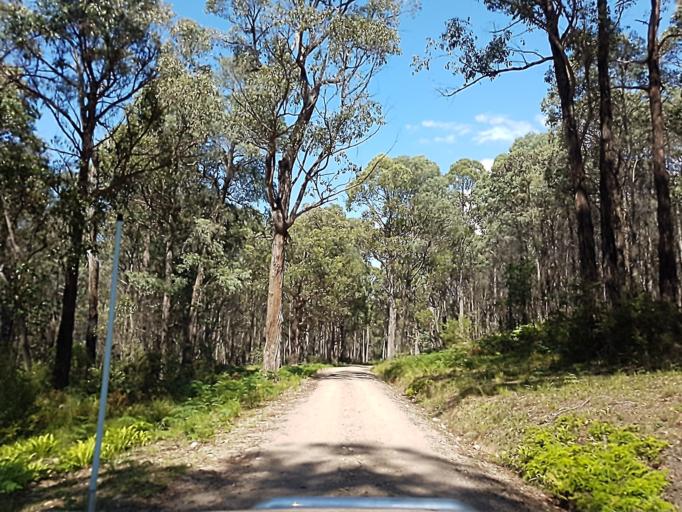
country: AU
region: Victoria
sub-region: East Gippsland
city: Lakes Entrance
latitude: -37.3010
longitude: 148.3267
